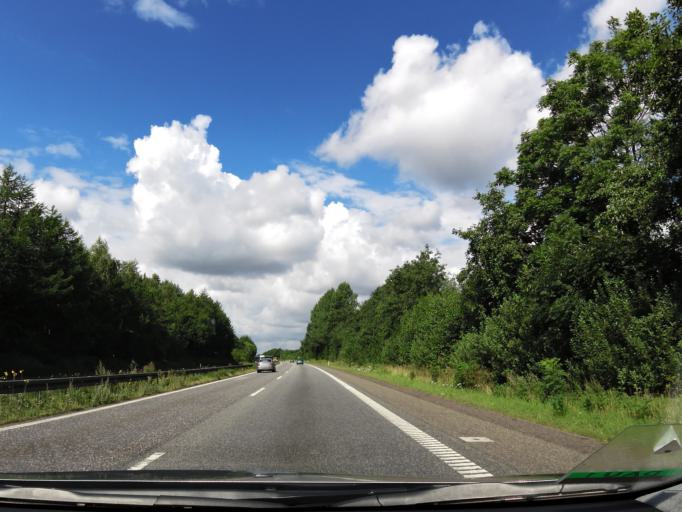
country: DK
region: South Denmark
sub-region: Odense Kommune
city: Bellinge
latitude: 55.3815
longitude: 10.2741
